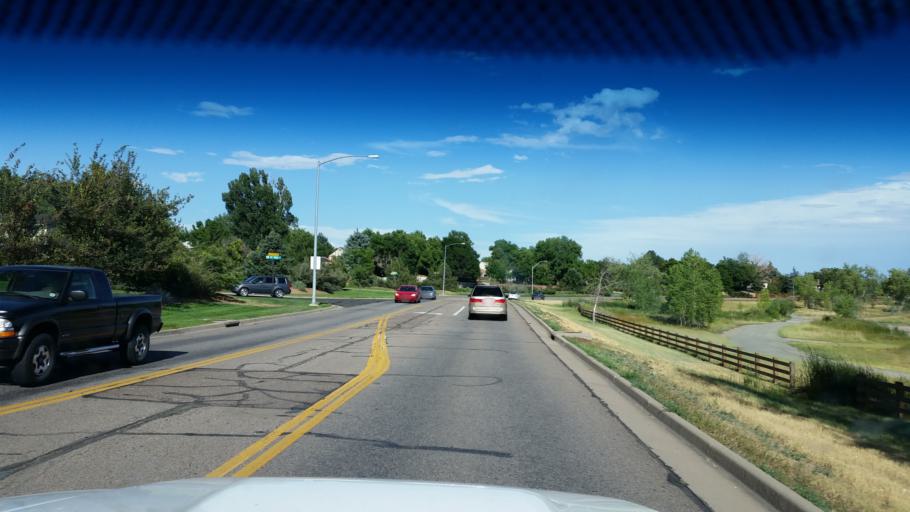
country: US
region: Colorado
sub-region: Adams County
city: Northglenn
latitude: 39.9291
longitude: -104.9520
